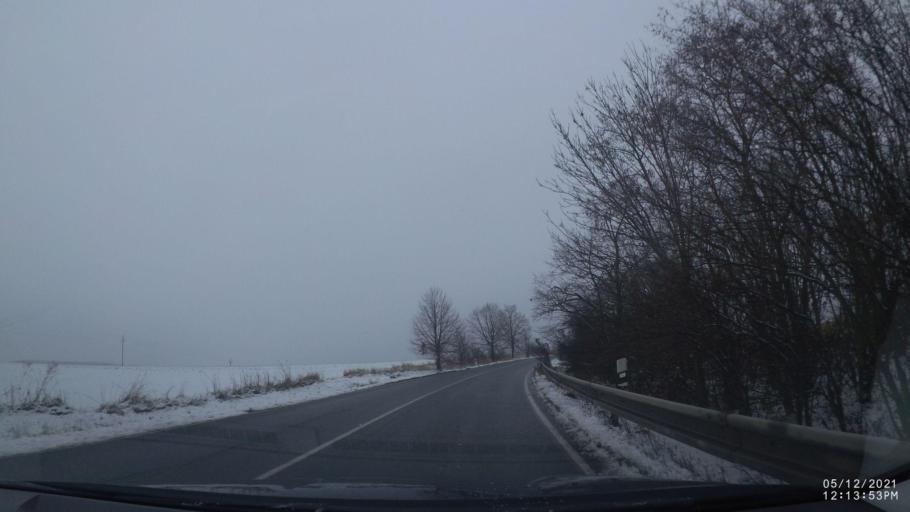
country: CZ
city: Ceske Mezirici
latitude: 50.3045
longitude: 16.0253
